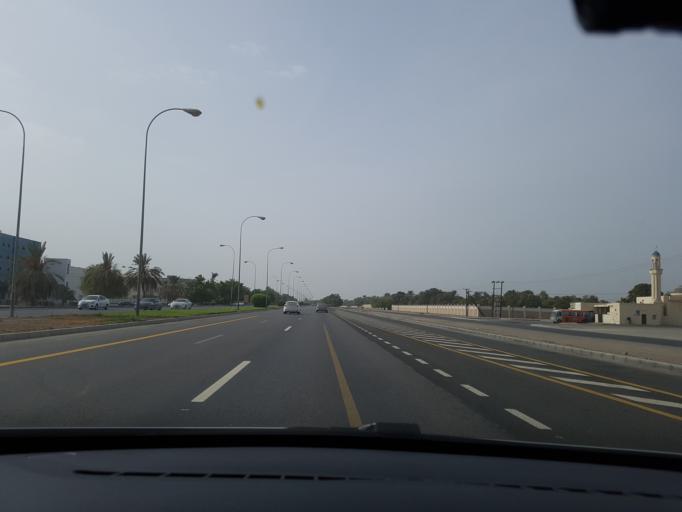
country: OM
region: Al Batinah
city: Al Sohar
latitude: 24.3811
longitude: 56.7020
